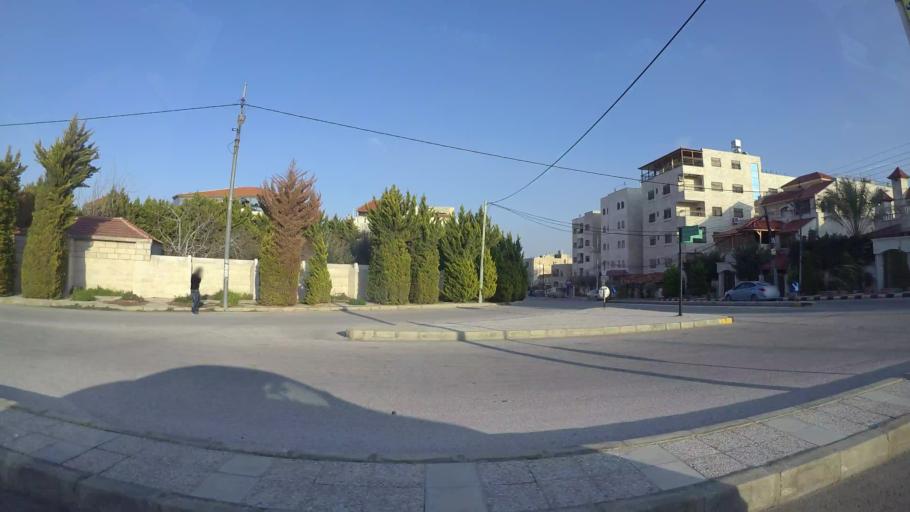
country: JO
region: Amman
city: Amman
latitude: 31.9866
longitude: 35.9578
